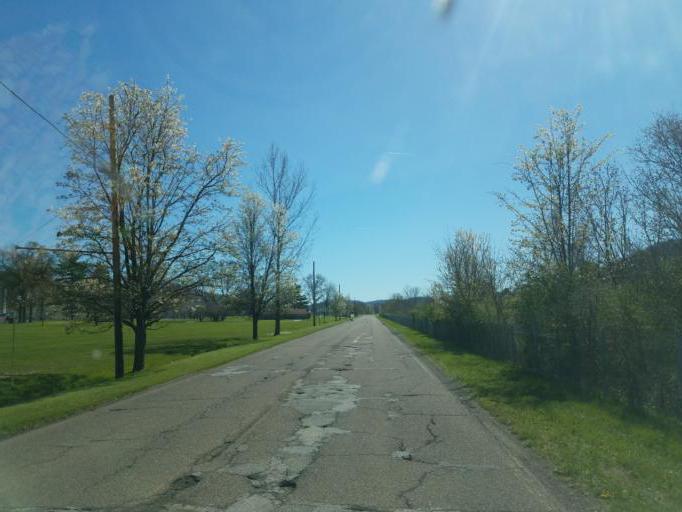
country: US
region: Ohio
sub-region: Jefferson County
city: Tiltonsville
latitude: 40.1853
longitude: -80.6874
